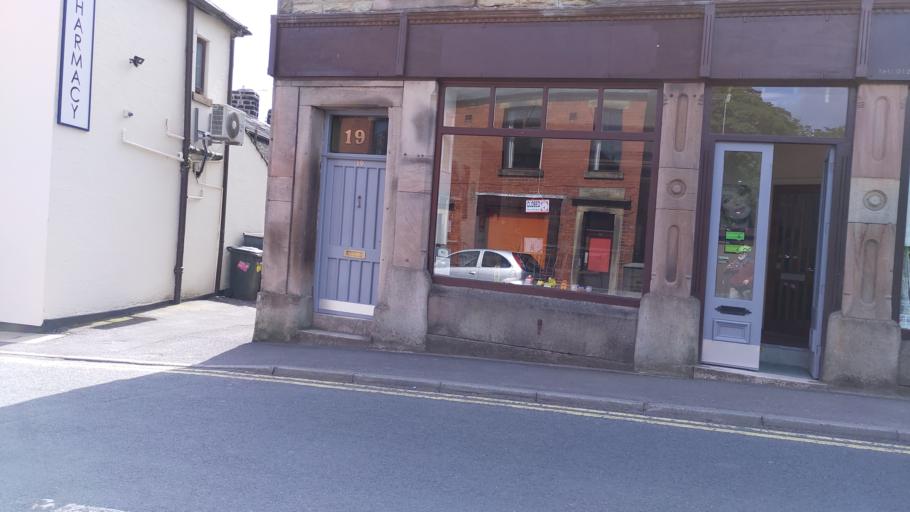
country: GB
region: England
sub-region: Lancashire
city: Chorley
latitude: 53.6934
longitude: -2.5567
